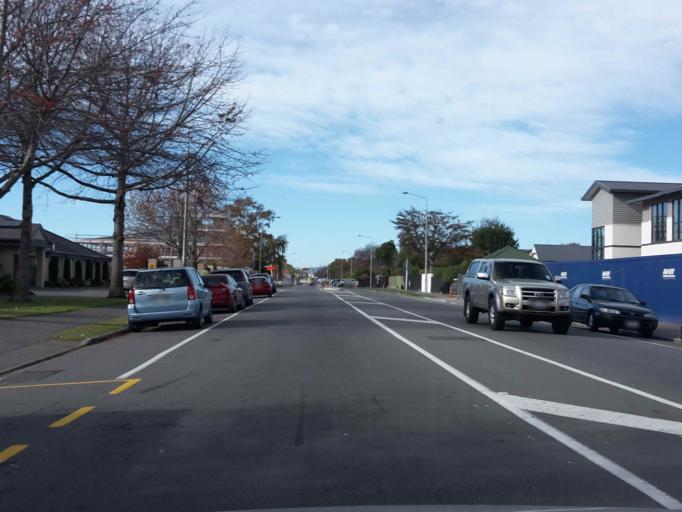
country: NZ
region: Canterbury
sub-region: Christchurch City
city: Christchurch
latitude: -43.4942
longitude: 172.6023
